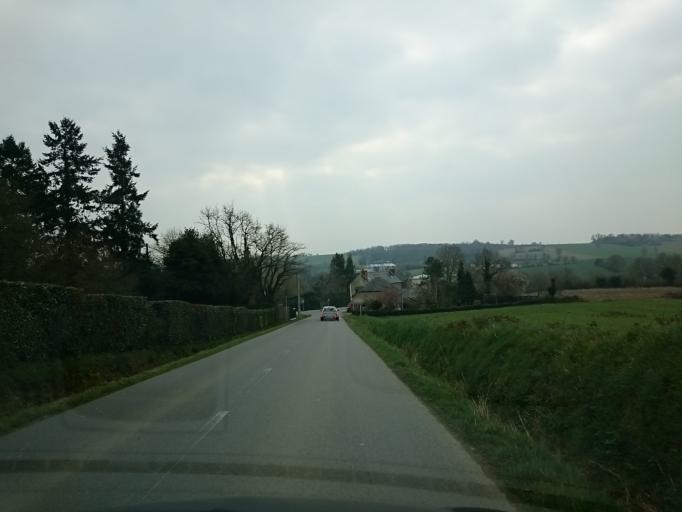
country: FR
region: Brittany
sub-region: Departement d'Ille-et-Vilaine
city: Pance
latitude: 47.8925
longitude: -1.6112
